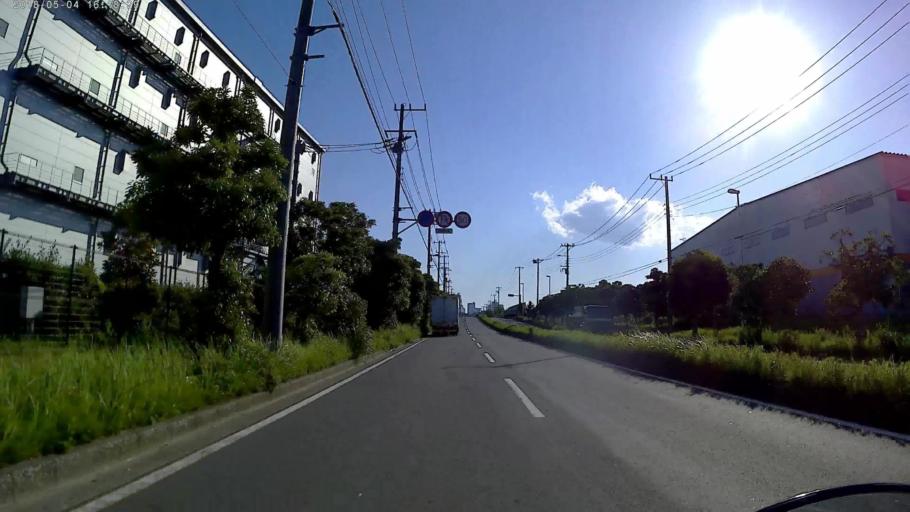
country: JP
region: Kanagawa
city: Yokohama
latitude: 35.4844
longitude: 139.6686
